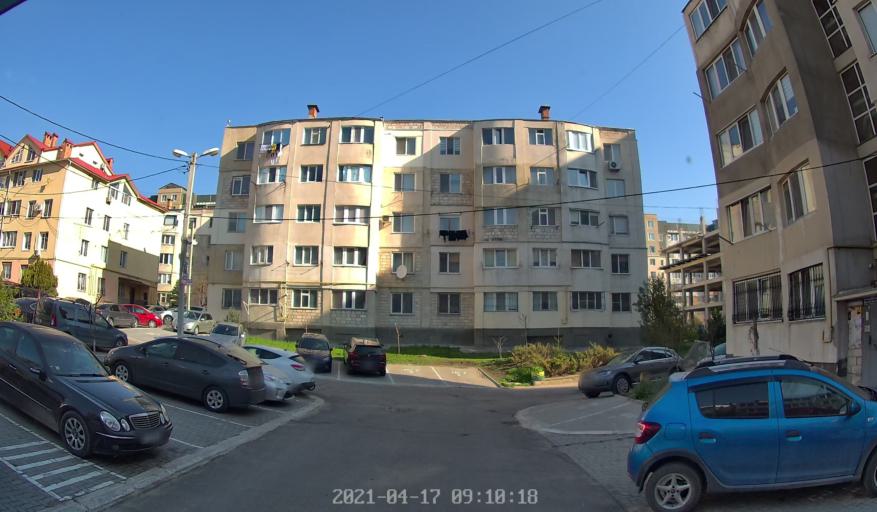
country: MD
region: Chisinau
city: Stauceni
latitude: 47.0474
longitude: 28.8955
